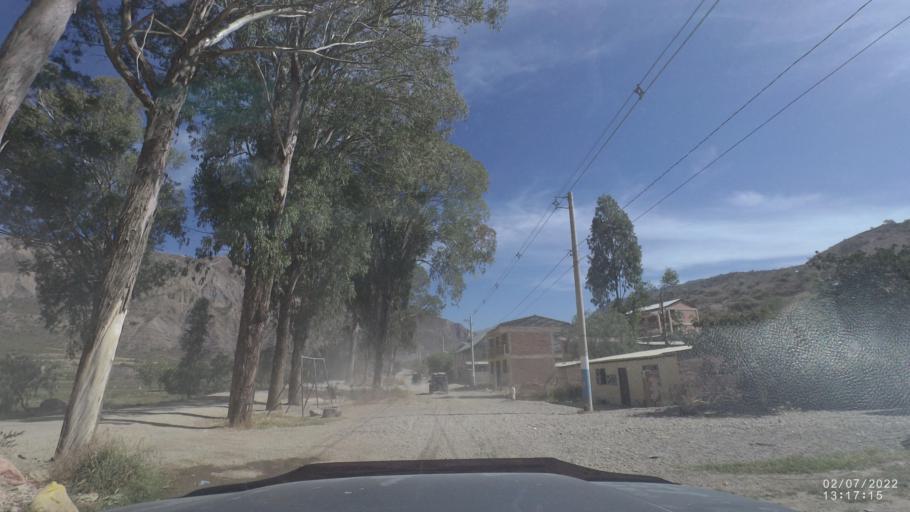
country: BO
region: Cochabamba
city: Irpa Irpa
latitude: -17.7325
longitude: -66.3090
